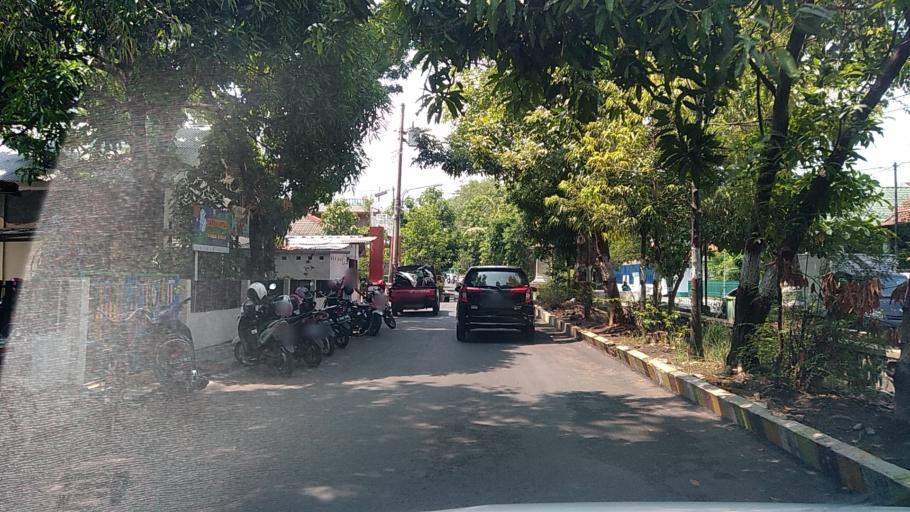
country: ID
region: Central Java
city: Semarang
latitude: -7.0074
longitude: 110.4393
